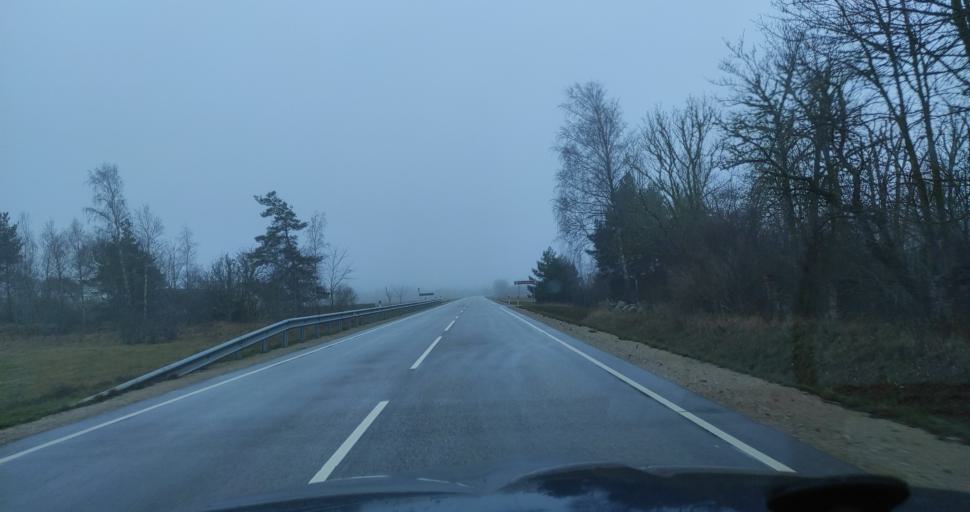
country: LV
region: Pavilostas
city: Pavilosta
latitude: 56.9354
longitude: 21.2756
